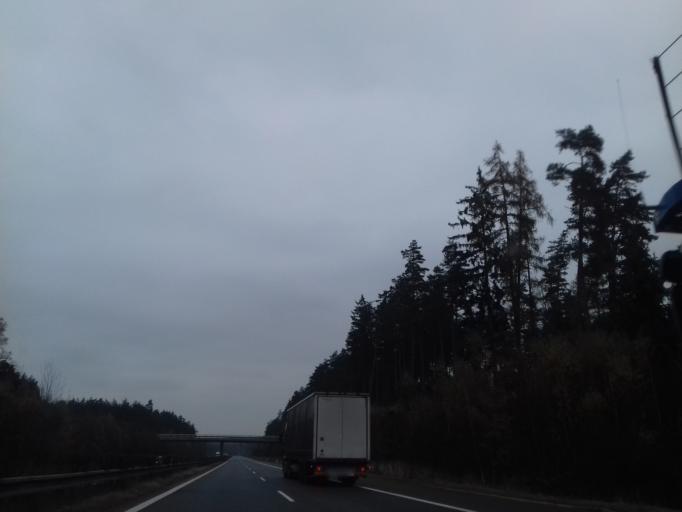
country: CZ
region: Plzensky
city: Line
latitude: 49.6945
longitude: 13.2952
